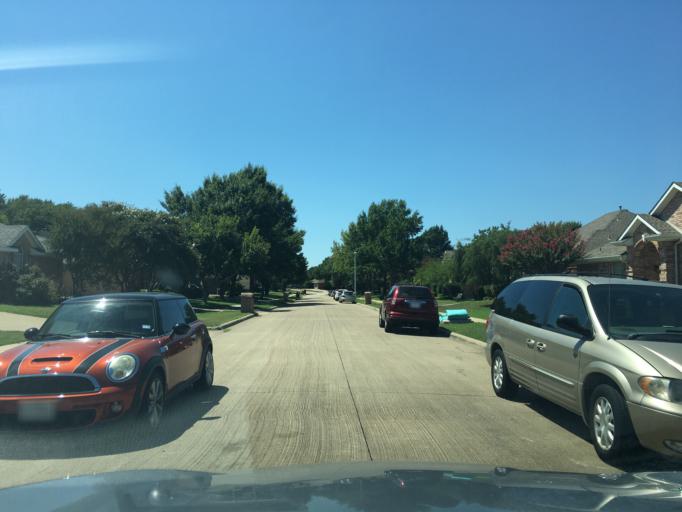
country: US
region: Texas
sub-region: Dallas County
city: Sachse
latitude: 32.9642
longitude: -96.6291
